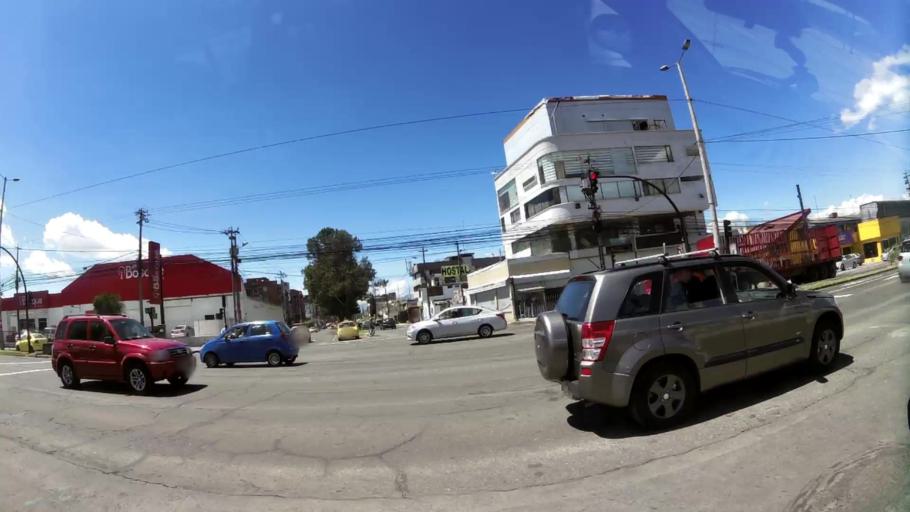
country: EC
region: Pichincha
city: Quito
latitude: -0.1534
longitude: -78.4847
